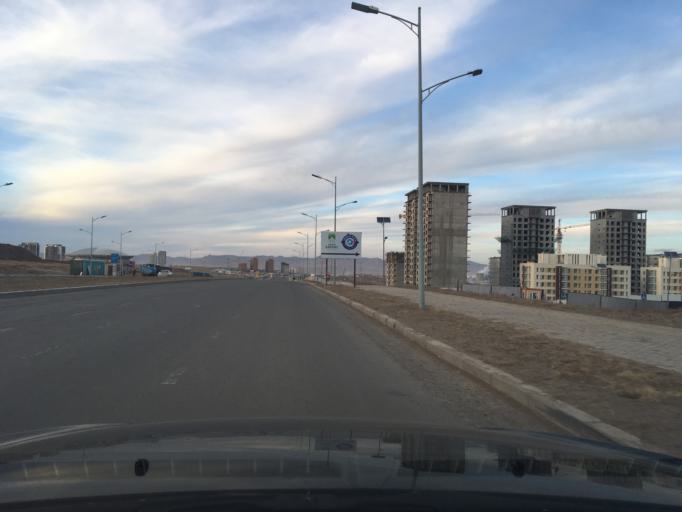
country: MN
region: Ulaanbaatar
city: Ulaanbaatar
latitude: 47.8461
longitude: 106.7908
